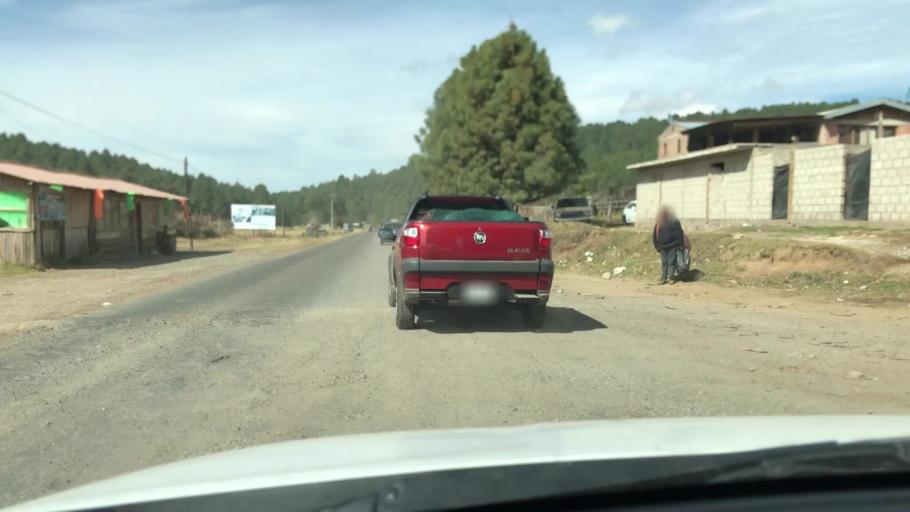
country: MX
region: Jalisco
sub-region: Amacueca
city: Tepec
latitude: 20.0371
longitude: -103.6896
